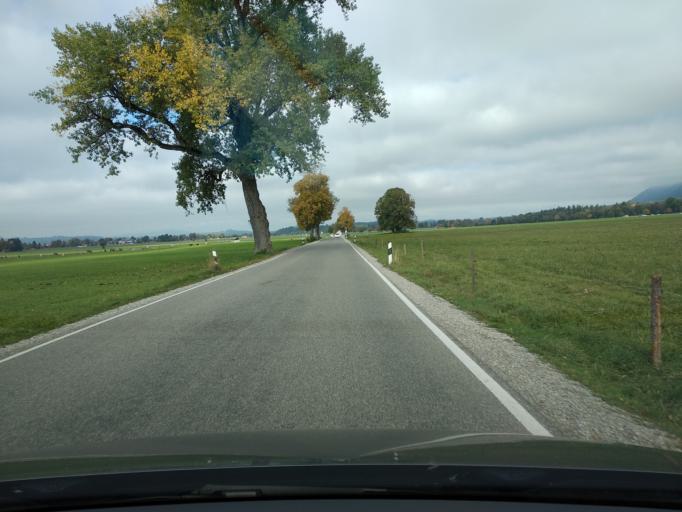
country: DE
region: Bavaria
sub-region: Swabia
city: Schwangau
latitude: 47.5664
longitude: 10.7436
